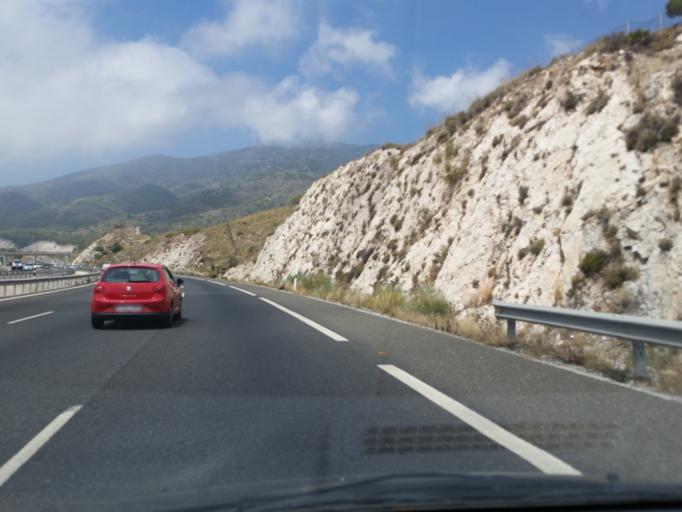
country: ES
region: Andalusia
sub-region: Provincia de Malaga
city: Benalmadena
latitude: 36.6068
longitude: -4.5561
